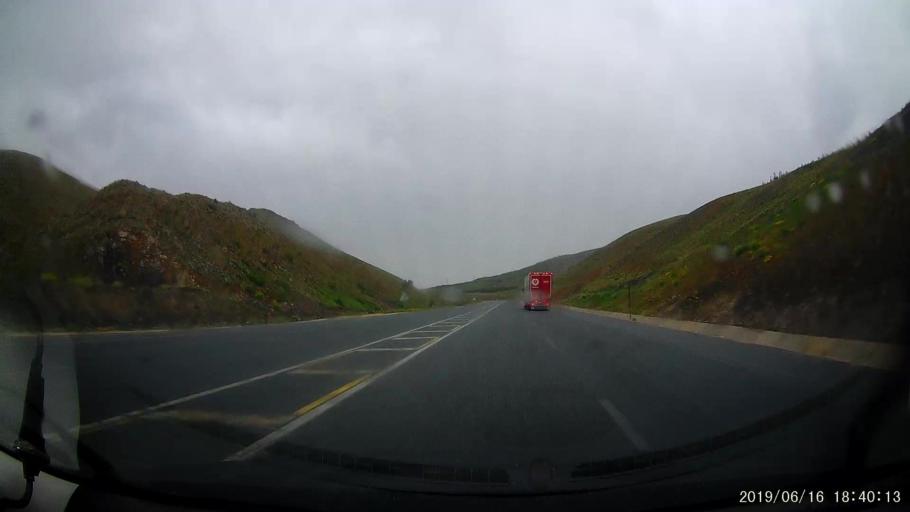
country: TR
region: Erzincan
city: Catalarmut
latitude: 39.8804
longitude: 39.1514
